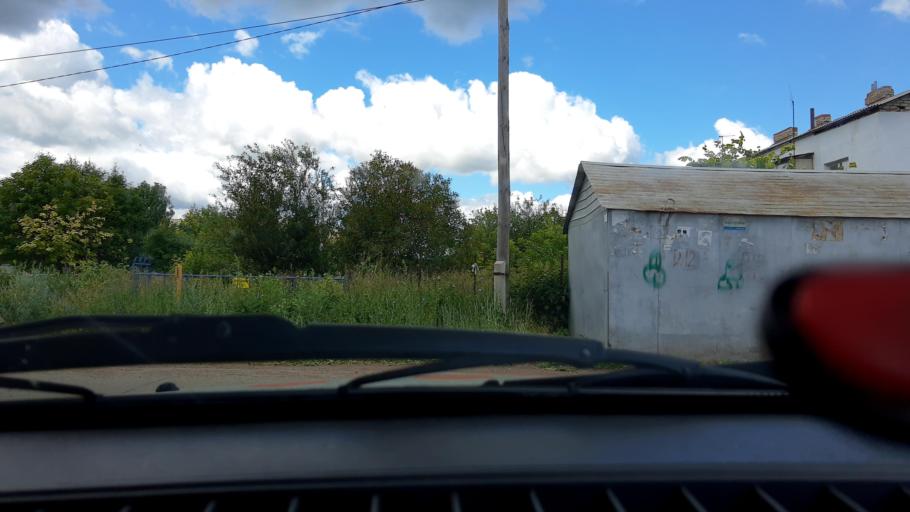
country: RU
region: Bashkortostan
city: Avdon
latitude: 54.6103
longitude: 55.8455
